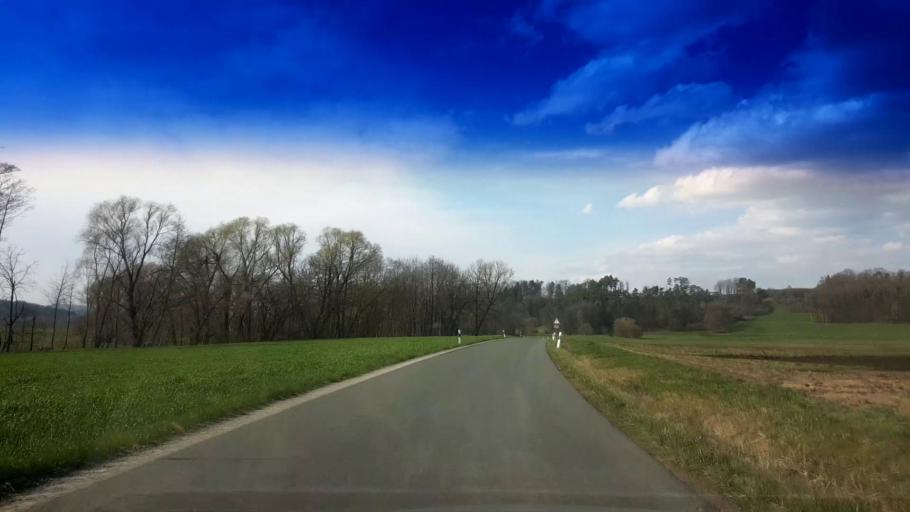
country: DE
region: Bavaria
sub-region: Upper Franconia
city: Gesees
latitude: 50.0284
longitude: 11.6404
